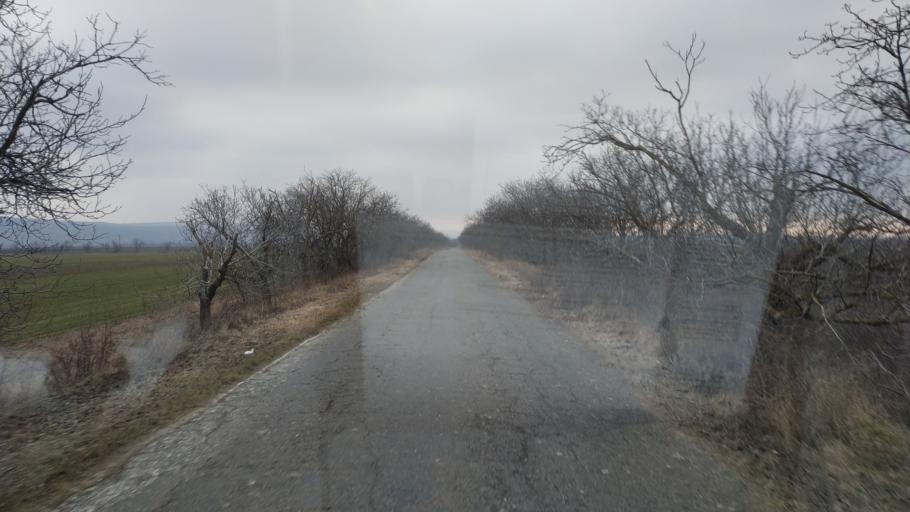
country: MD
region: Hincesti
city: Dancu
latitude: 46.8885
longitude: 28.3012
